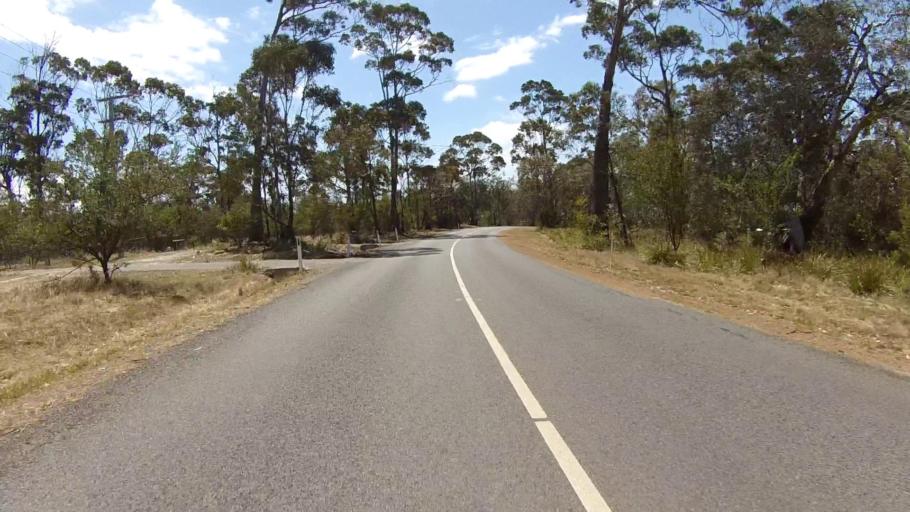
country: AU
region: Tasmania
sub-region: Clarence
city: Sandford
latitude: -43.0016
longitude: 147.4754
